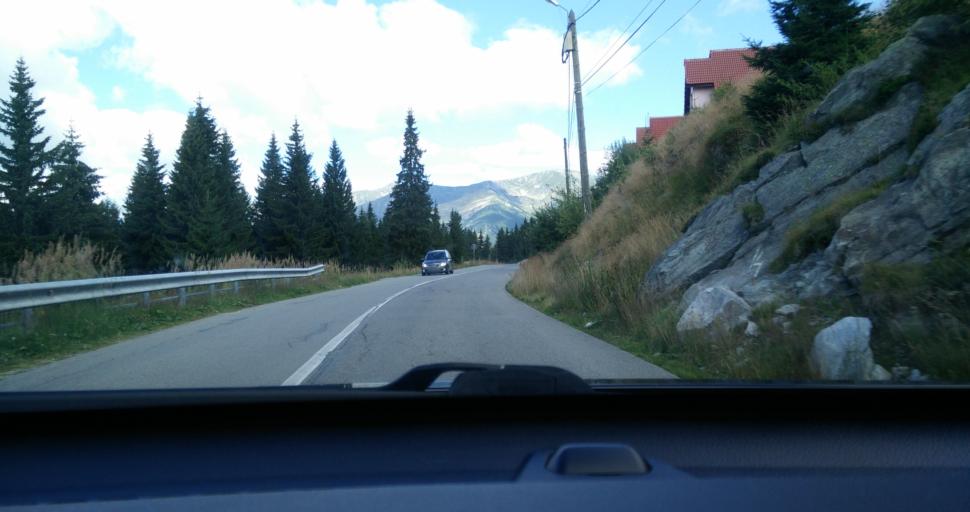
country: RO
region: Gorj
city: Novaci-Straini
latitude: 45.2883
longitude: 23.6911
